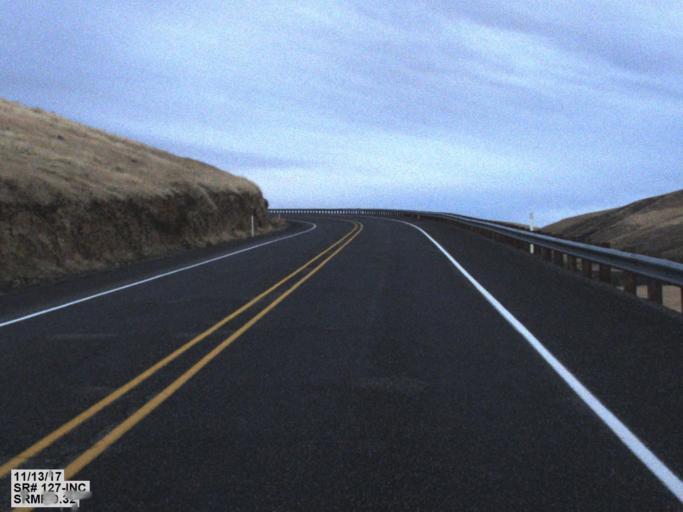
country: US
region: Washington
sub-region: Garfield County
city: Pomeroy
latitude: 46.5228
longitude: -117.8164
